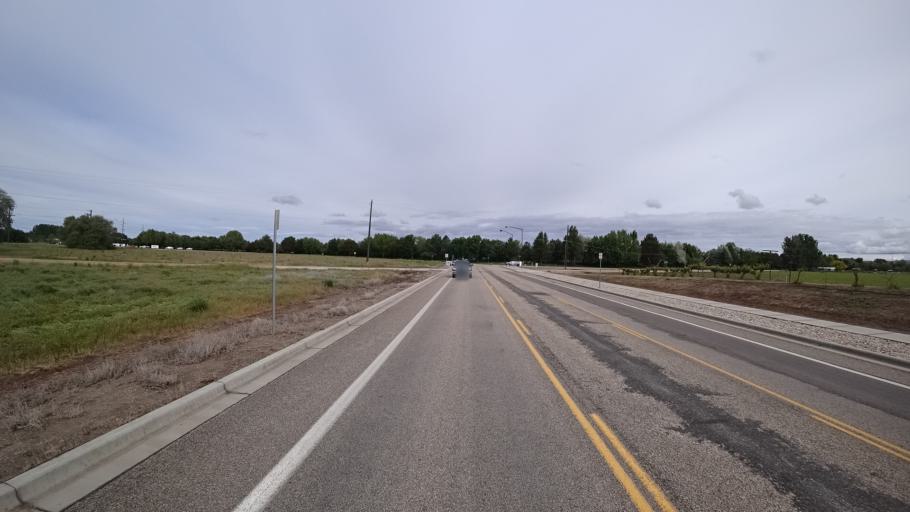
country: US
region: Idaho
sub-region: Ada County
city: Eagle
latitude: 43.6964
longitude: -116.3787
